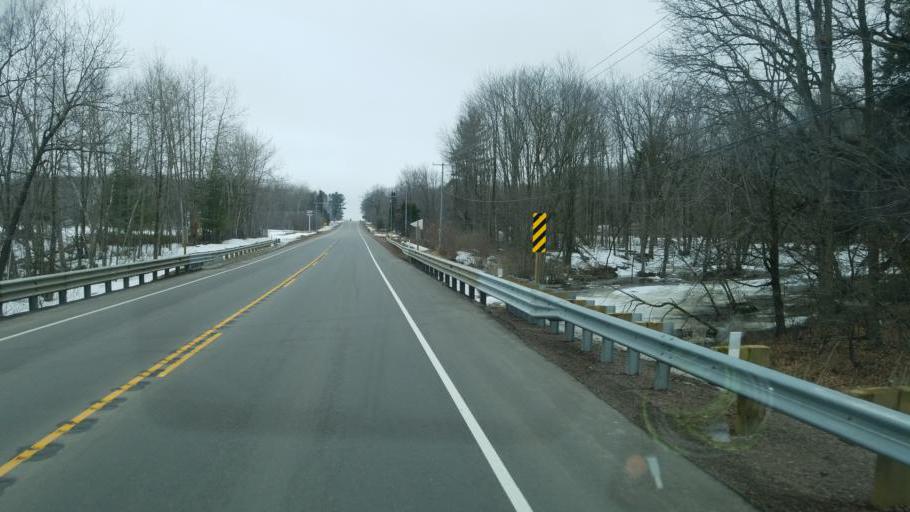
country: US
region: Wisconsin
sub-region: Wood County
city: Marshfield
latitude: 44.6564
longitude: -90.2537
